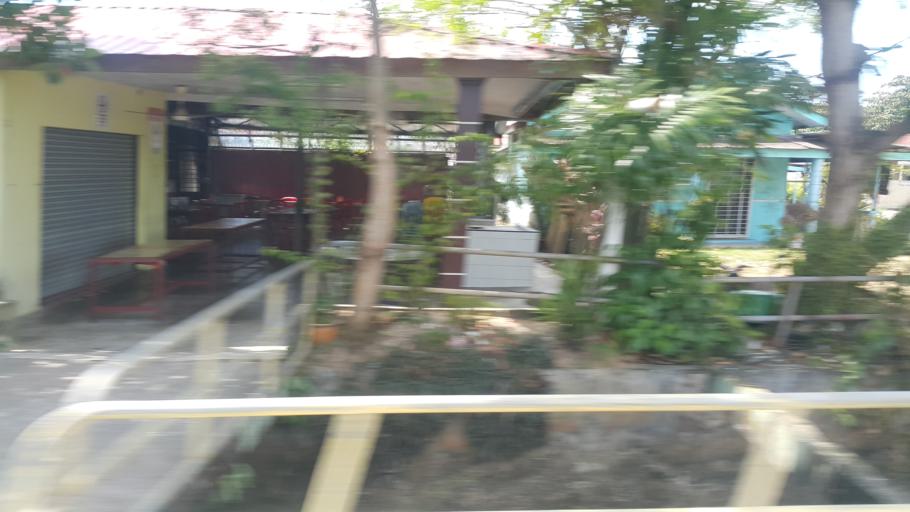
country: MY
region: Melaka
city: Kampung Bukit Baharu
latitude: 2.1864
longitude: 102.2757
